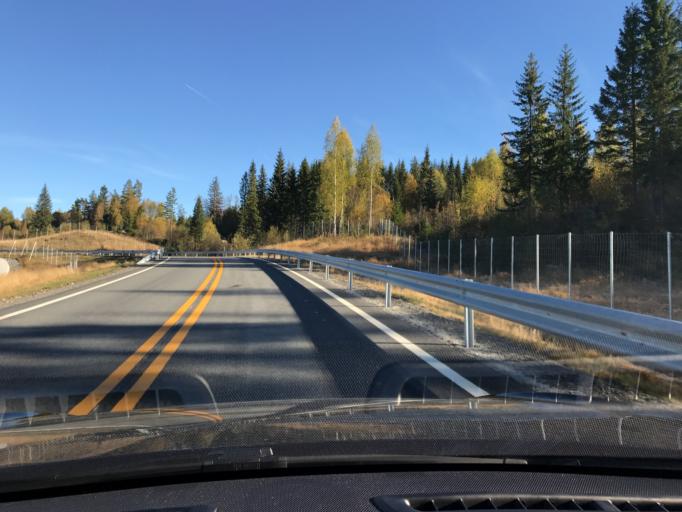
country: NO
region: Buskerud
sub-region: Krodsherad
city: Noresund
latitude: 60.2660
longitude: 9.7938
